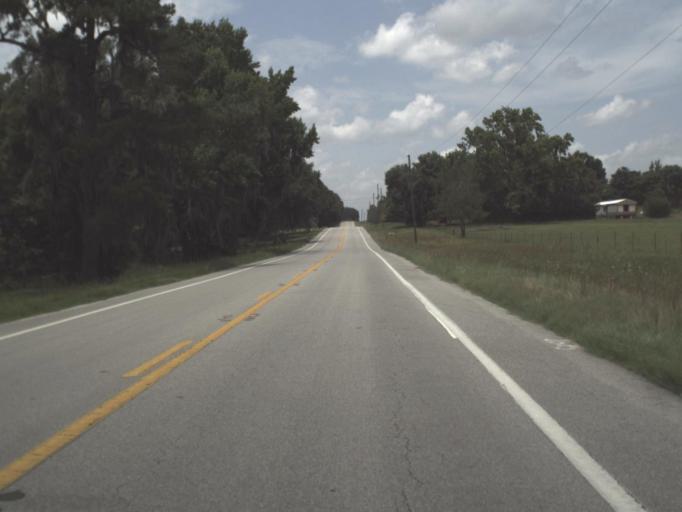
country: US
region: Florida
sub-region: Madison County
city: Madison
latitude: 30.5173
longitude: -83.4225
